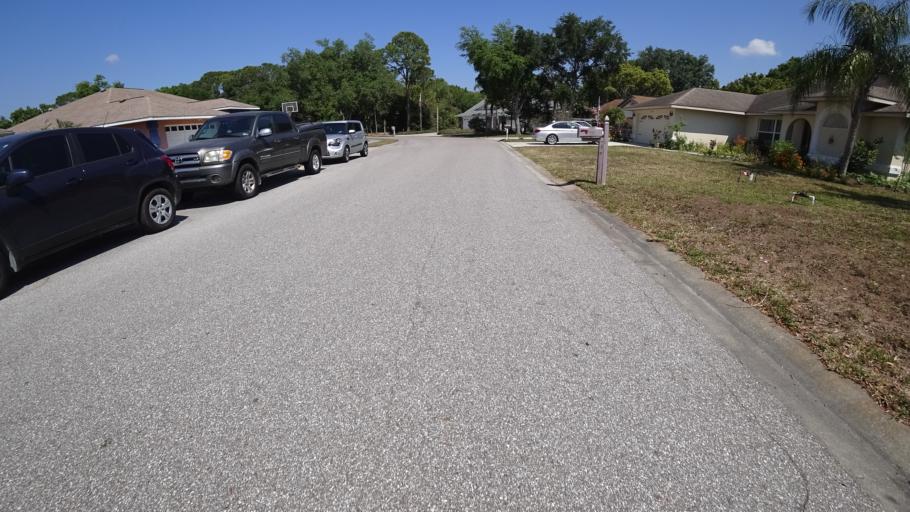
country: US
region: Florida
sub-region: Manatee County
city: Samoset
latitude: 27.4574
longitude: -82.5182
